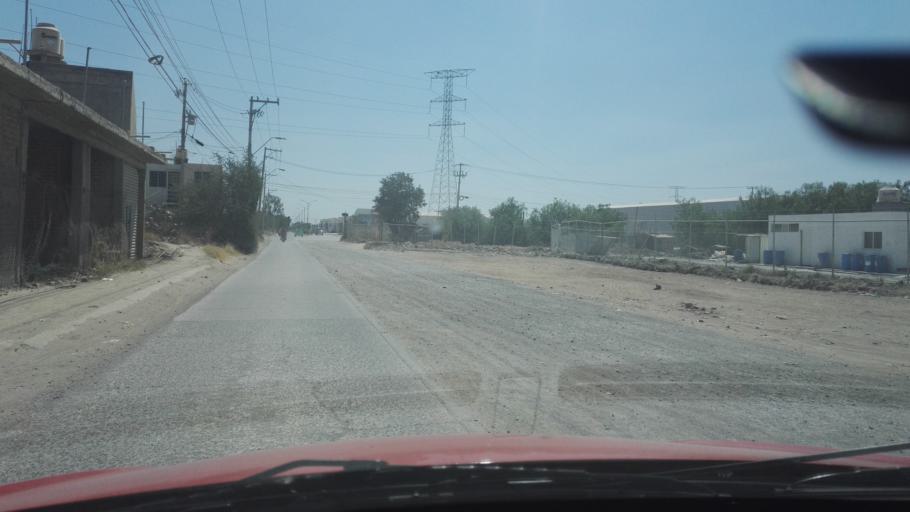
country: MX
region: Guanajuato
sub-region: Leon
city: Fraccionamiento Paraiso Real
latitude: 21.0915
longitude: -101.5966
